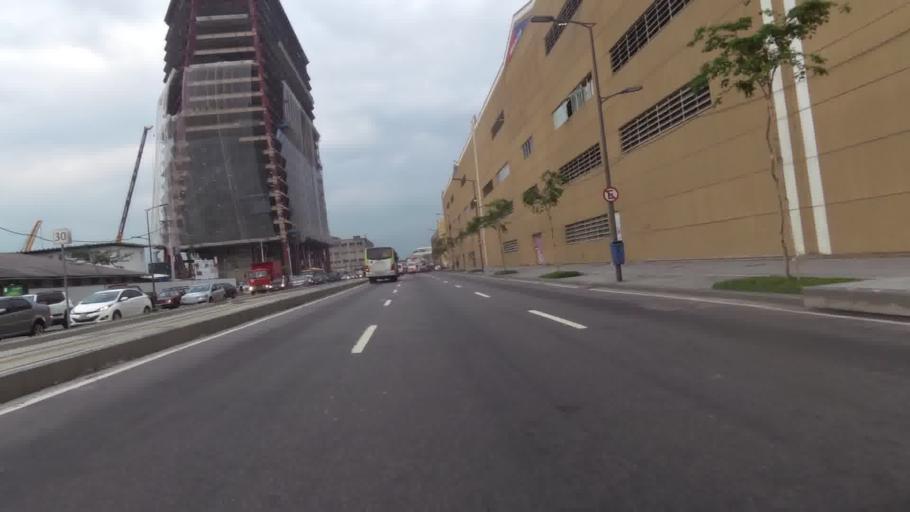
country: BR
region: Rio de Janeiro
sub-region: Rio De Janeiro
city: Rio de Janeiro
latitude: -22.8949
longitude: -43.1984
